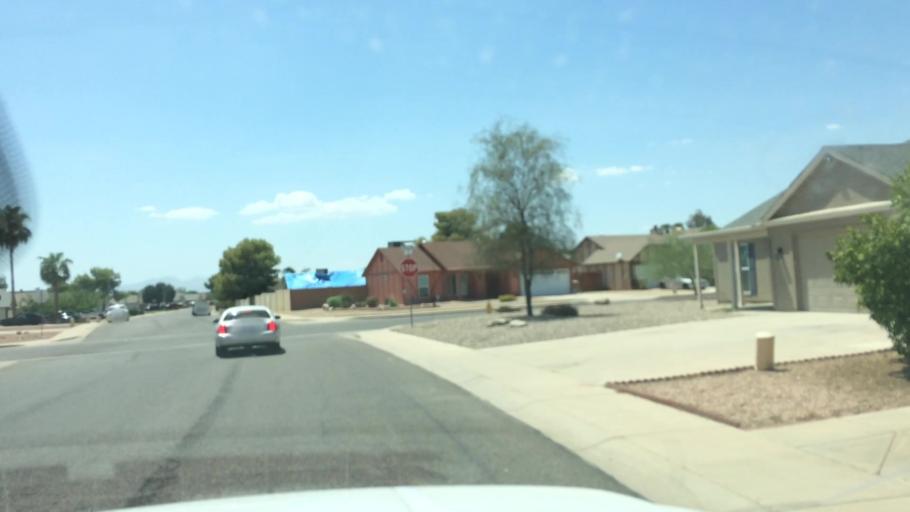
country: US
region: Arizona
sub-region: Maricopa County
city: Peoria
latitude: 33.5984
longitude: -112.2412
